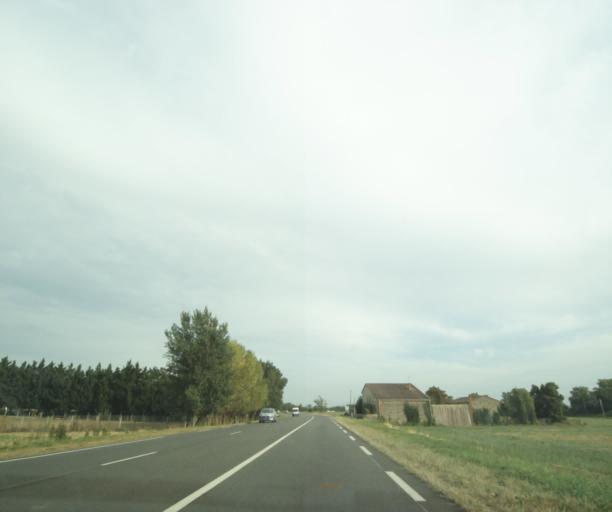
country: FR
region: Midi-Pyrenees
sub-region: Departement de la Haute-Garonne
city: Castelnau-d'Estretefonds
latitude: 43.7950
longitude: 1.3358
